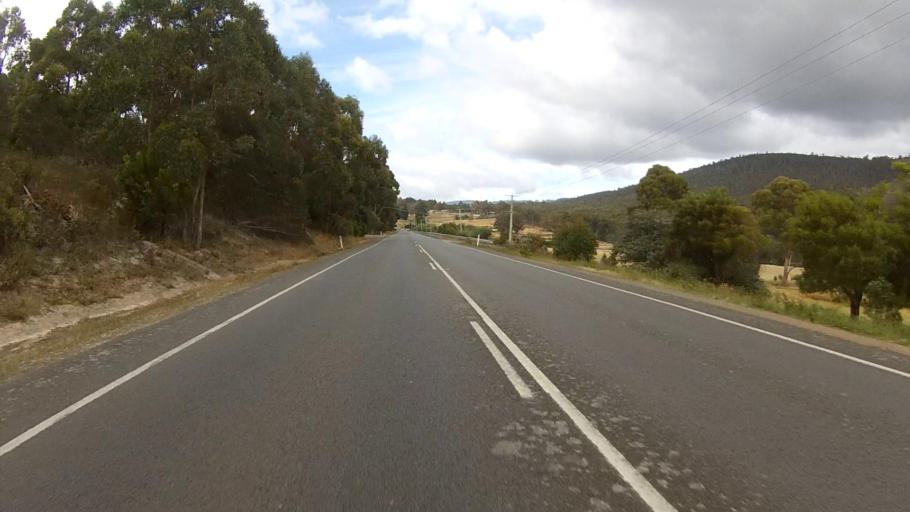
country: AU
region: Tasmania
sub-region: Kingborough
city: Kettering
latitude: -43.0805
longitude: 147.2549
